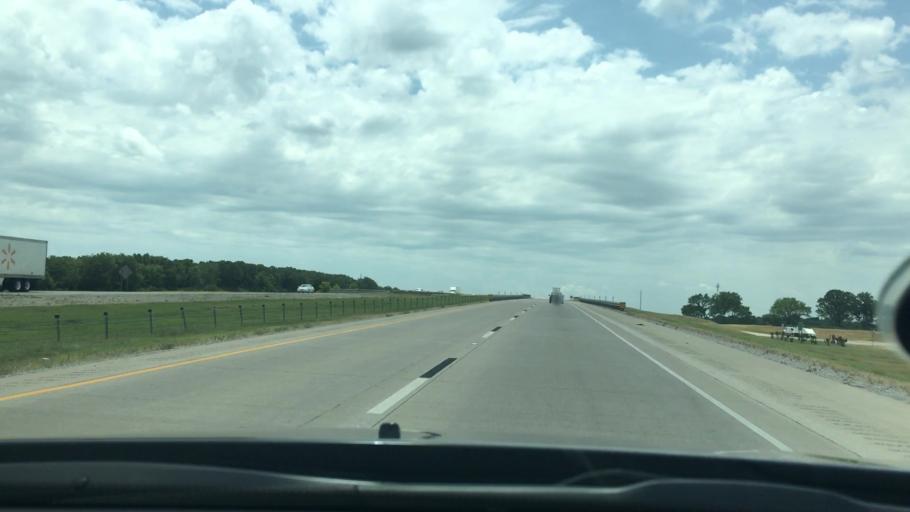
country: US
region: Oklahoma
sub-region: Carter County
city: Ardmore
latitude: 34.1414
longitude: -97.1558
